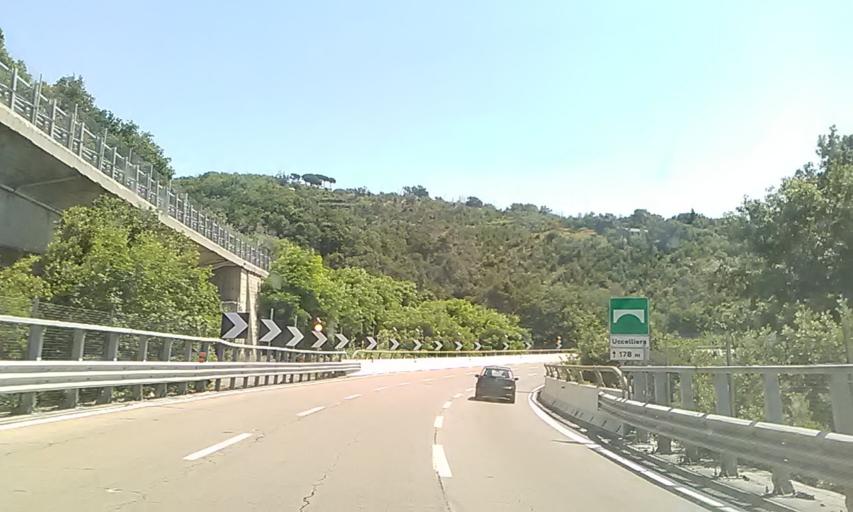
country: IT
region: Liguria
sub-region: Provincia di Genova
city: Arenzano
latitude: 44.4196
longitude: 8.7141
